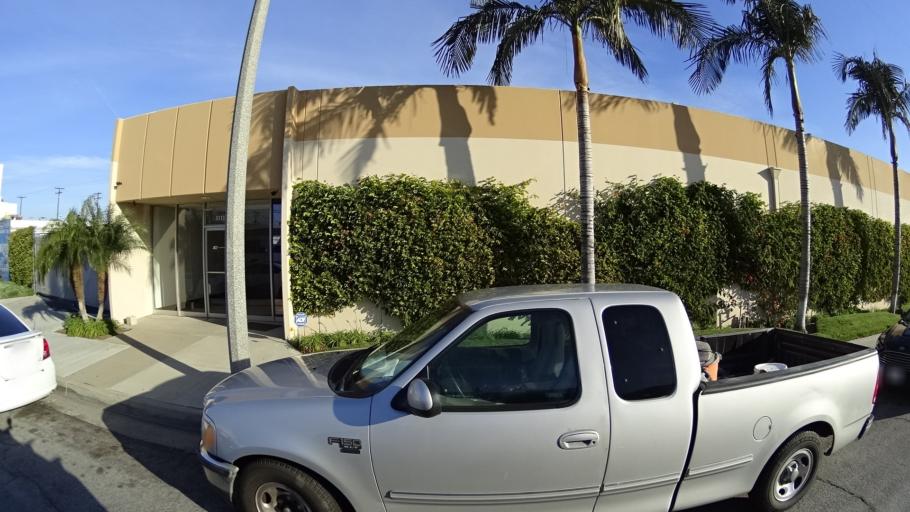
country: US
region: California
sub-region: Orange County
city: Fullerton
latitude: 33.8628
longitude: -117.9081
